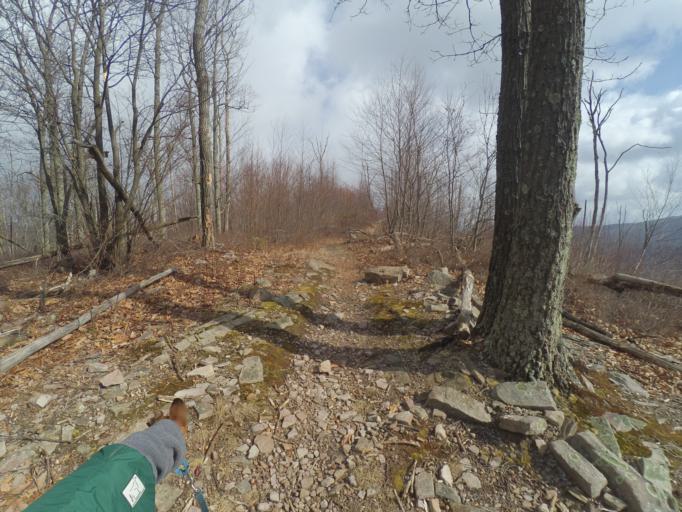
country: US
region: Pennsylvania
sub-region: Centre County
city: Boalsburg
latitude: 40.7498
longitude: -77.7345
